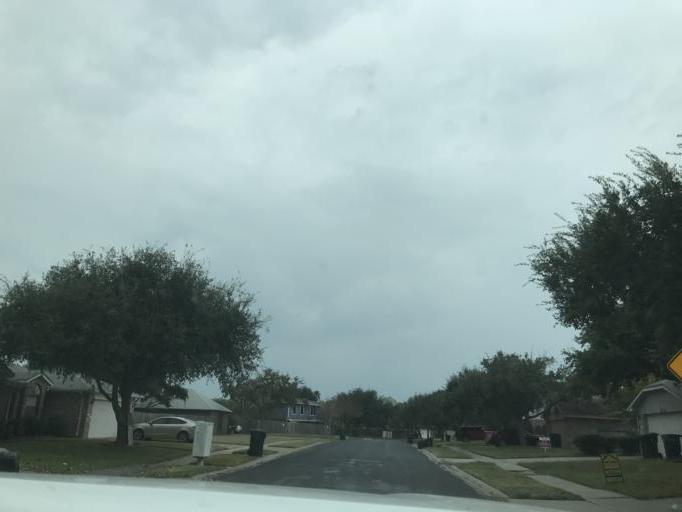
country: US
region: Texas
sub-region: Nueces County
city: Corpus Christi
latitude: 27.6712
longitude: -97.3476
